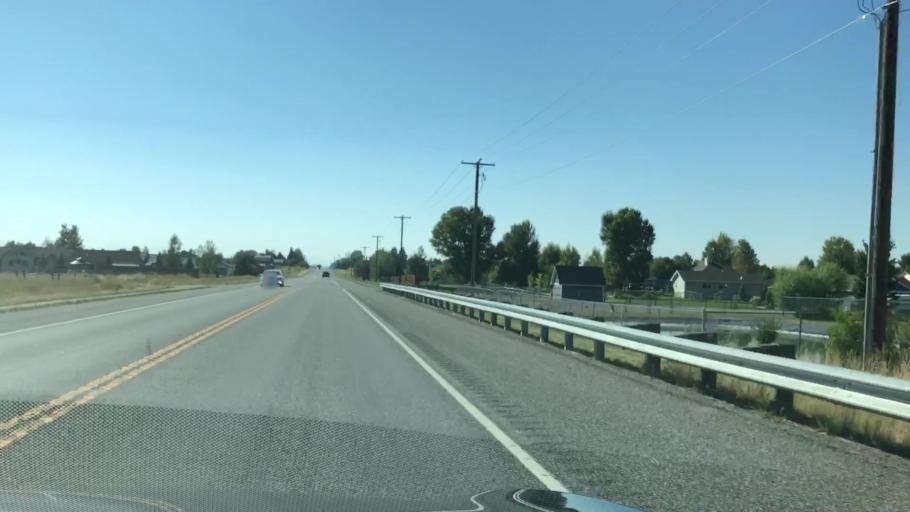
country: US
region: Montana
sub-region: Gallatin County
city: Belgrade
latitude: 45.7293
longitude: -111.1273
